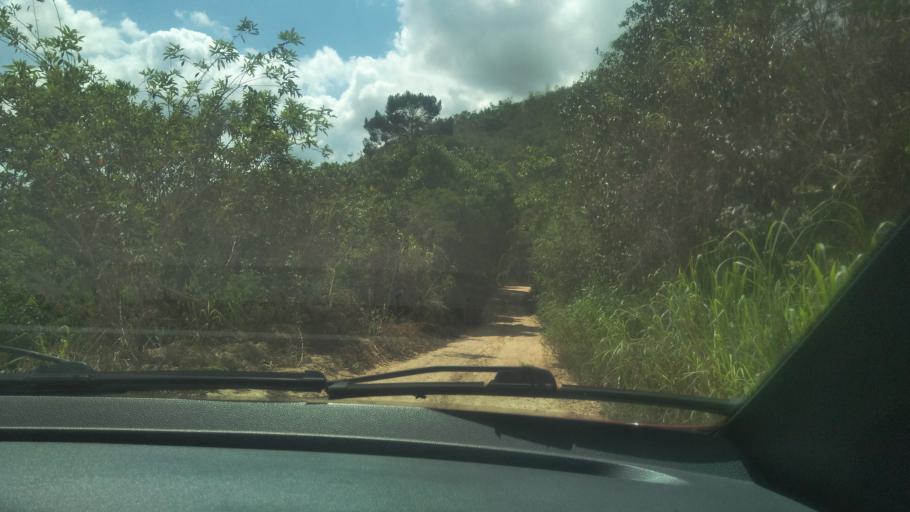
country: BR
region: Pernambuco
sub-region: Vitoria De Santo Antao
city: Vitoria de Santo Antao
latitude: -8.1438
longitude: -35.2642
